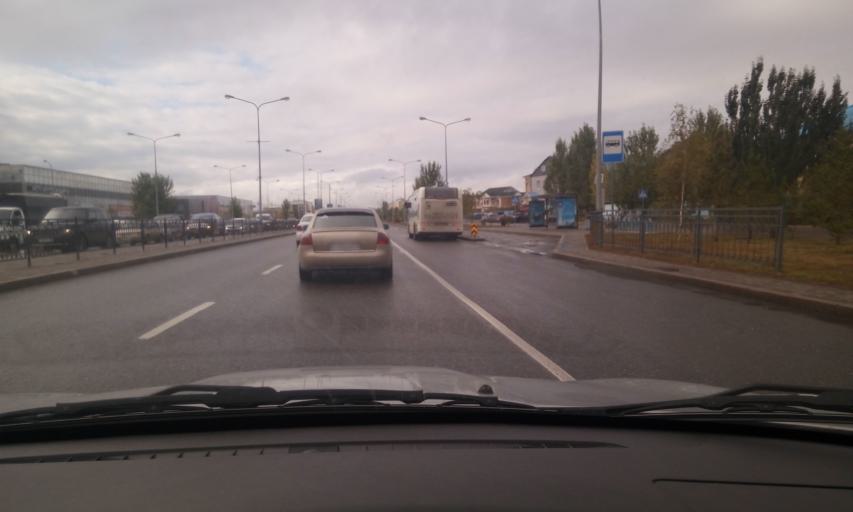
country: KZ
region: Astana Qalasy
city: Astana
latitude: 51.1462
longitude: 71.4053
